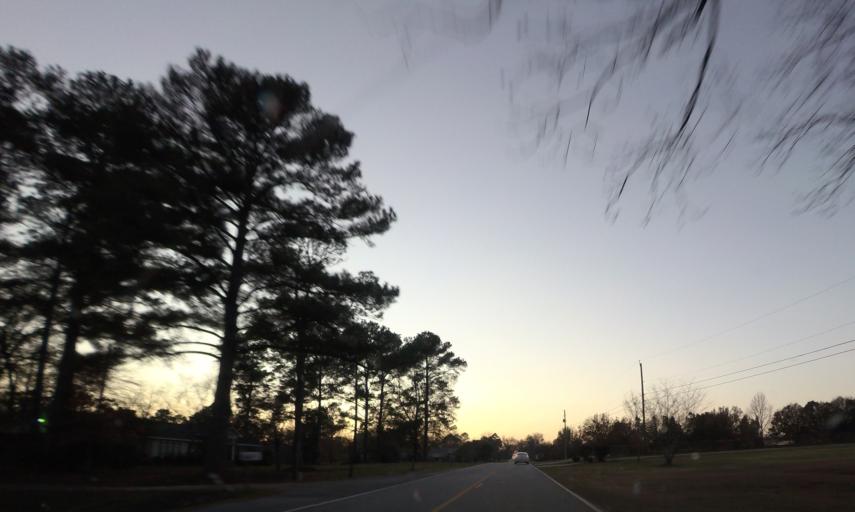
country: US
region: Georgia
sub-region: Houston County
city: Centerville
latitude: 32.7249
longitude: -83.6693
